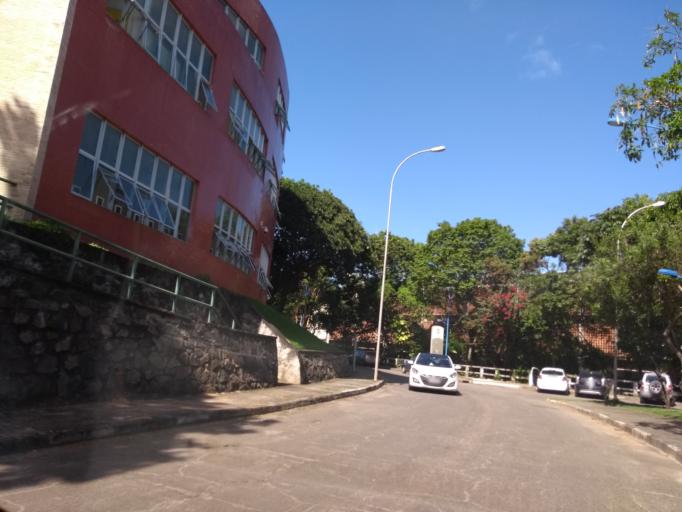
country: BR
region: Bahia
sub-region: Salvador
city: Salvador
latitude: -12.9986
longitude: -38.5087
